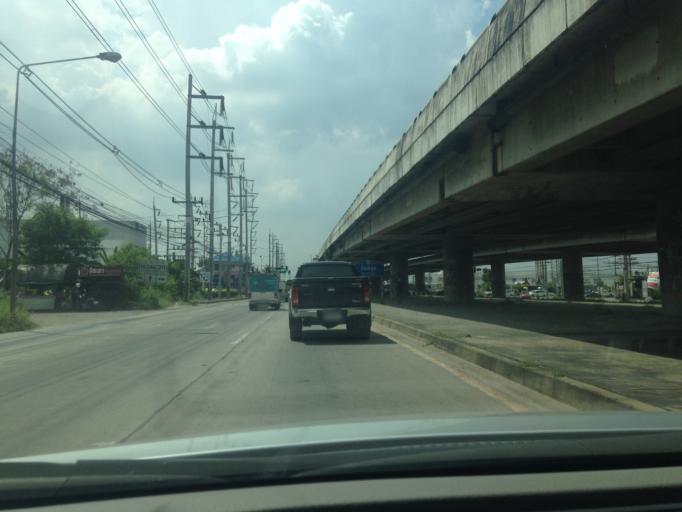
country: TH
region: Pathum Thani
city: Pathum Thani
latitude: 14.0298
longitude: 100.5271
